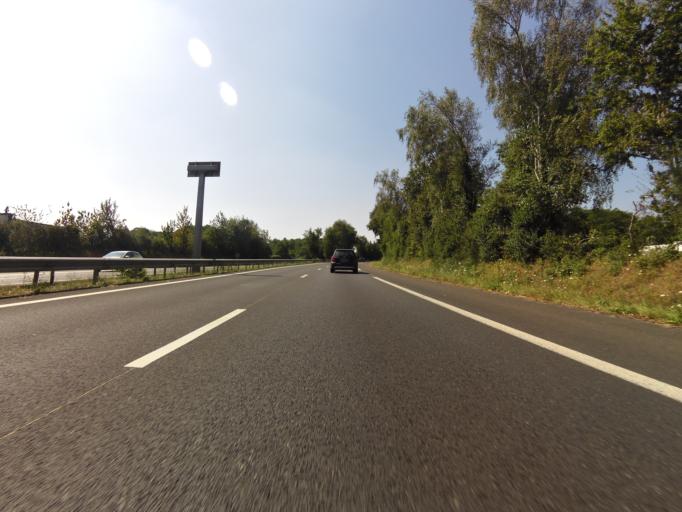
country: FR
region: Brittany
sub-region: Departement du Finistere
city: Plomelin
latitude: 47.9670
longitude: -4.1469
